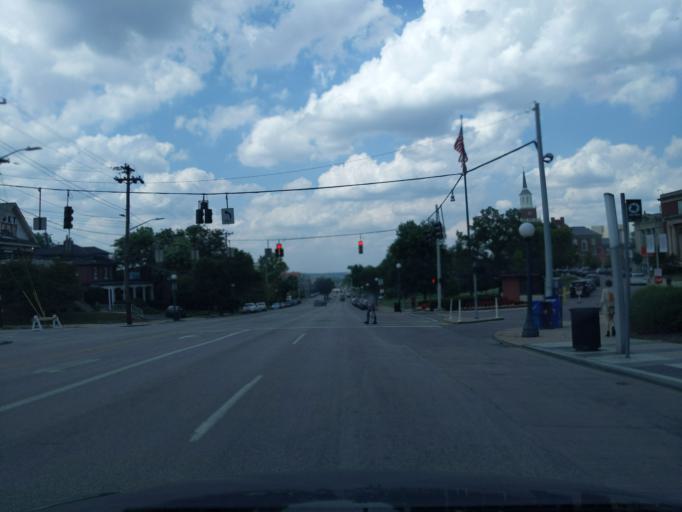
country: US
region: Ohio
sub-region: Hamilton County
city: Saint Bernard
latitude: 39.1293
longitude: -84.5206
